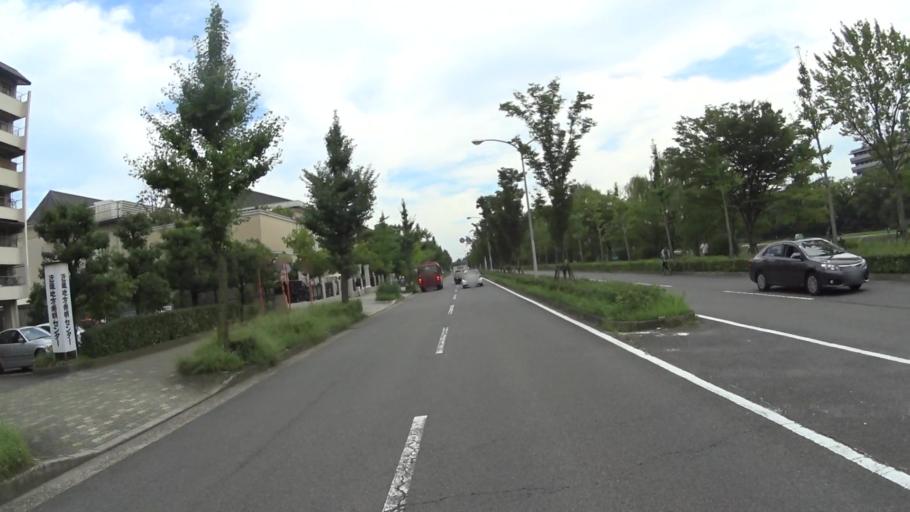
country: JP
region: Kyoto
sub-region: Kyoto-shi
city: Kamigyo-ku
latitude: 35.0246
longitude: 135.7722
